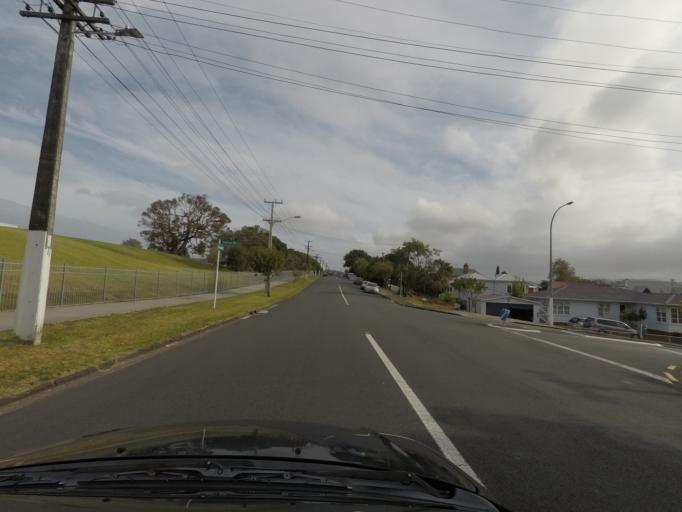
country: NZ
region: Auckland
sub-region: Auckland
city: Waitakere
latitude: -36.9040
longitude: 174.6647
